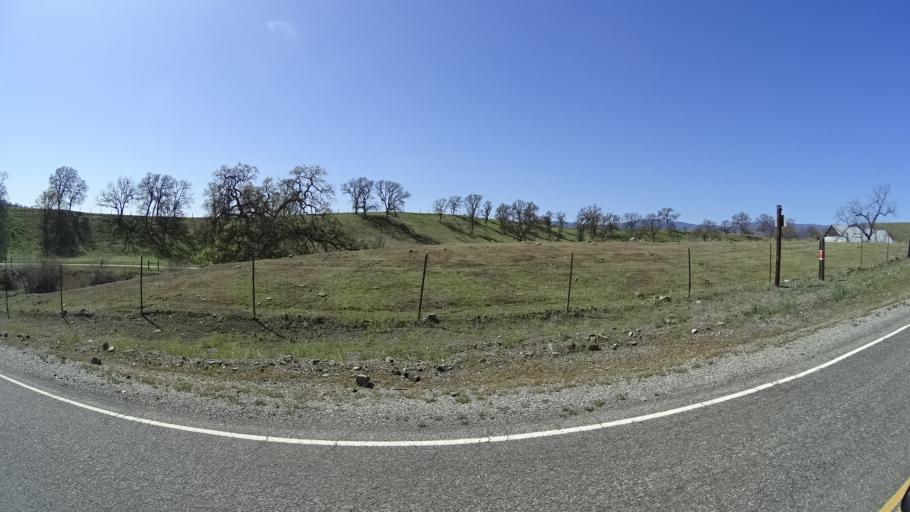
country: US
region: California
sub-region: Glenn County
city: Orland
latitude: 39.6831
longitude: -122.5367
